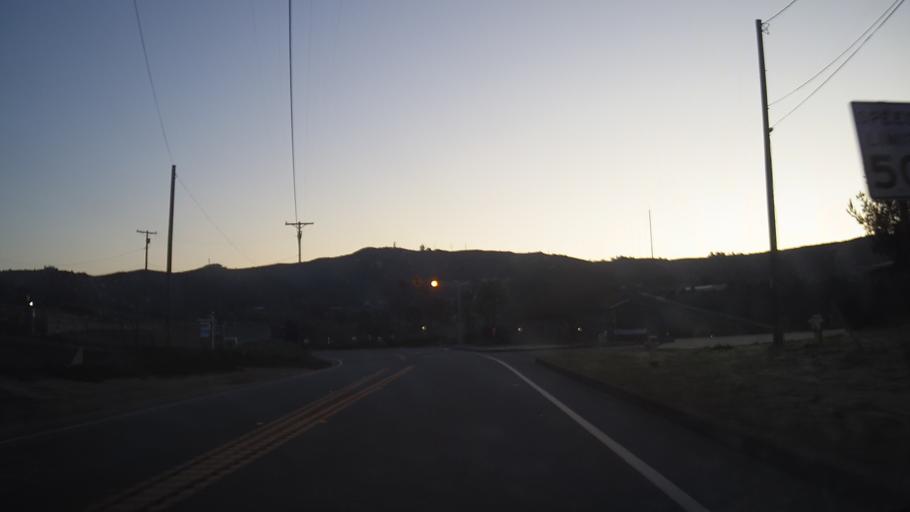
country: US
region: California
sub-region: San Diego County
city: Harbison Canyon
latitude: 32.7910
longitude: -116.8333
